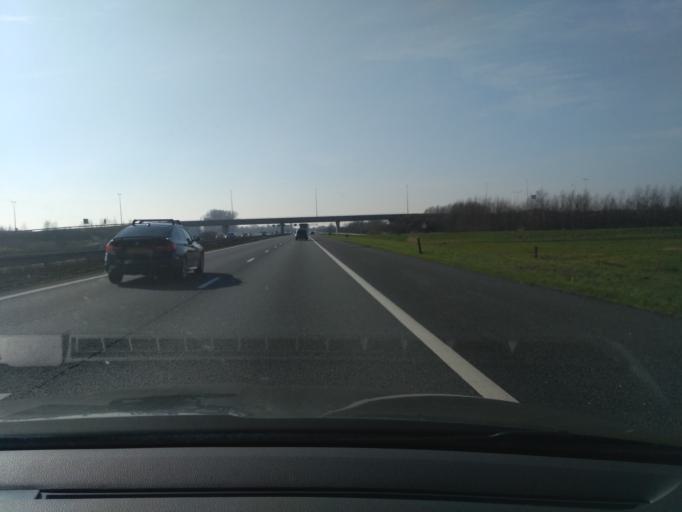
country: NL
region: Gelderland
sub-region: Gemeente Nijkerk
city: Nijkerk
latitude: 52.2126
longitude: 5.4452
